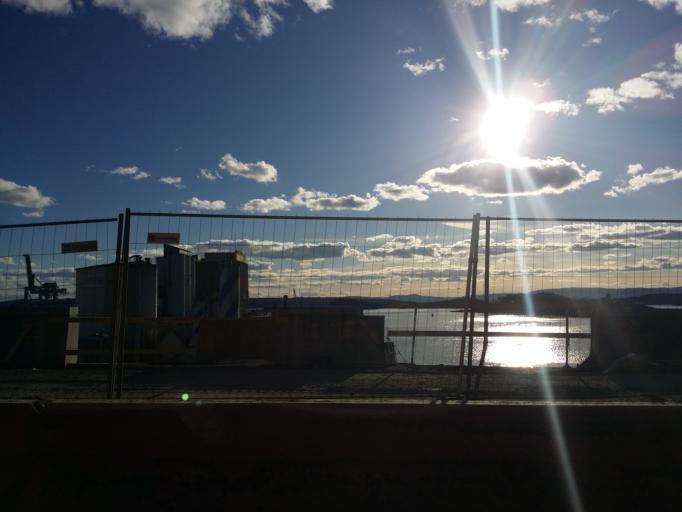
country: NO
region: Oslo
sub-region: Oslo
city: Oslo
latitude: 59.8918
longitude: 10.7605
